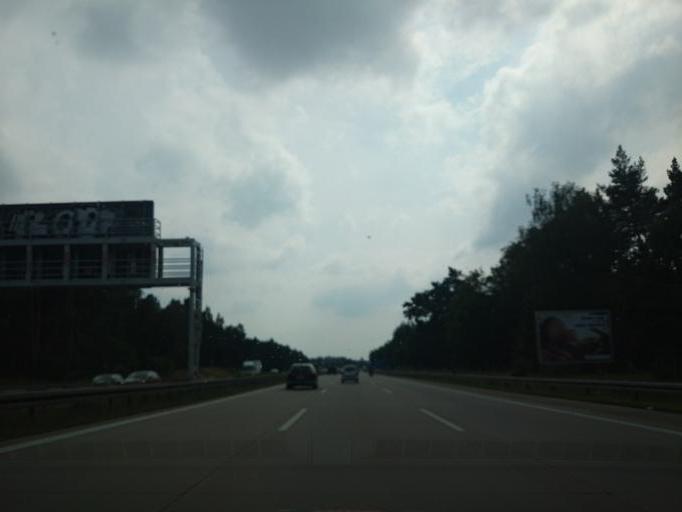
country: DE
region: Berlin
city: Wannsee
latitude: 52.3491
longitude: 13.1407
